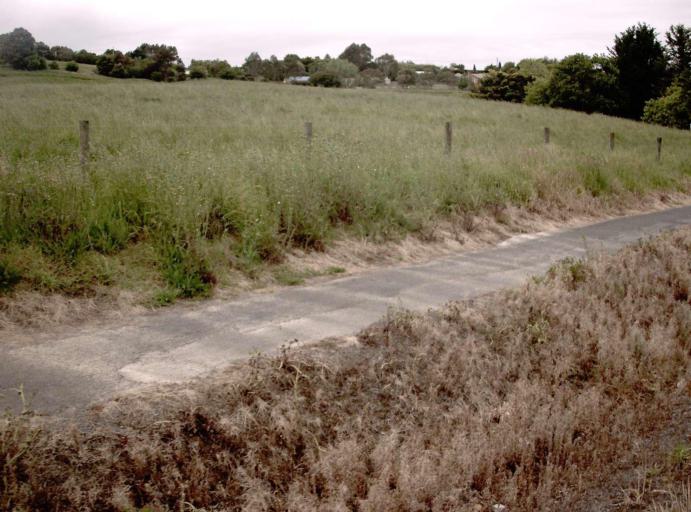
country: AU
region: Victoria
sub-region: Bass Coast
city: North Wonthaggi
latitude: -38.4420
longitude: 145.8088
